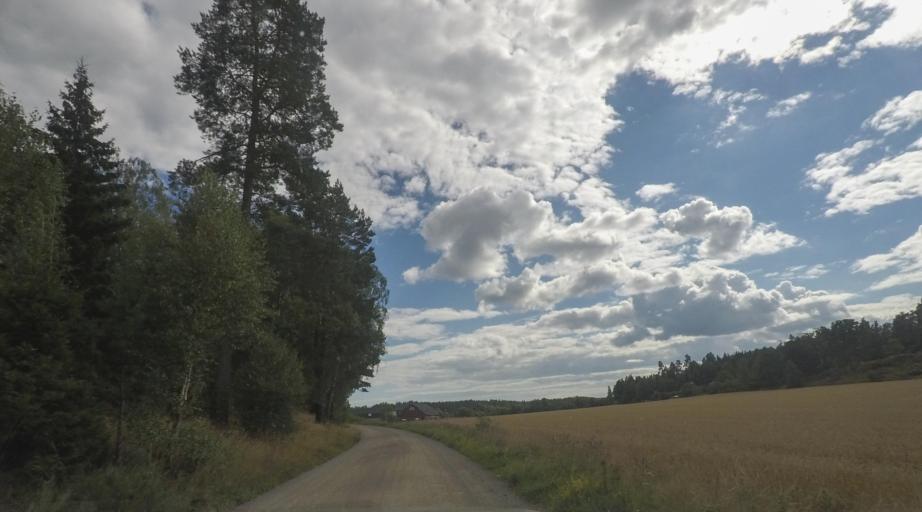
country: SE
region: Stockholm
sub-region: Sodertalje Kommun
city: Pershagen
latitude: 59.1166
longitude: 17.6570
